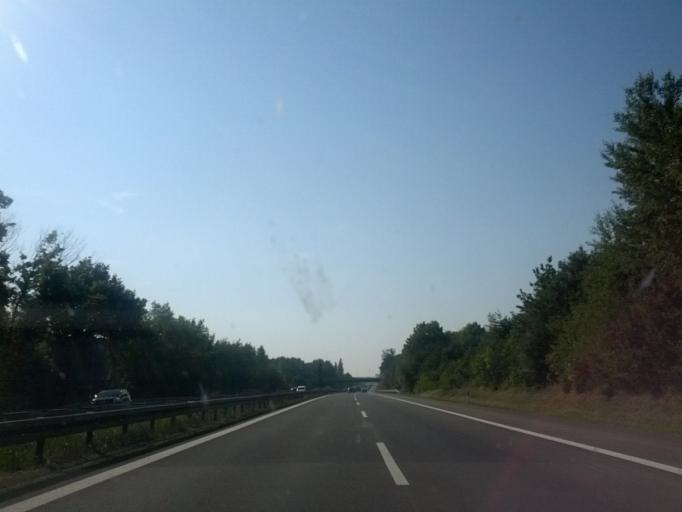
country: DE
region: Brandenburg
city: Bernau bei Berlin
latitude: 52.6852
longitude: 13.5613
